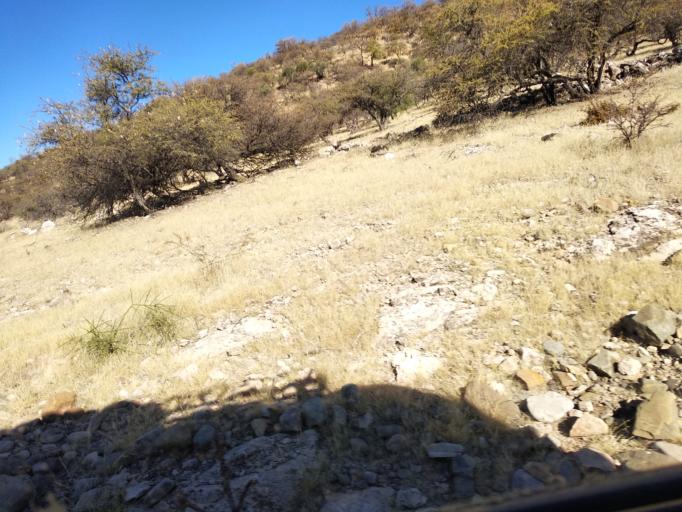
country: BO
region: Cochabamba
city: Mizque
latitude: -18.0836
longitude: -65.7508
